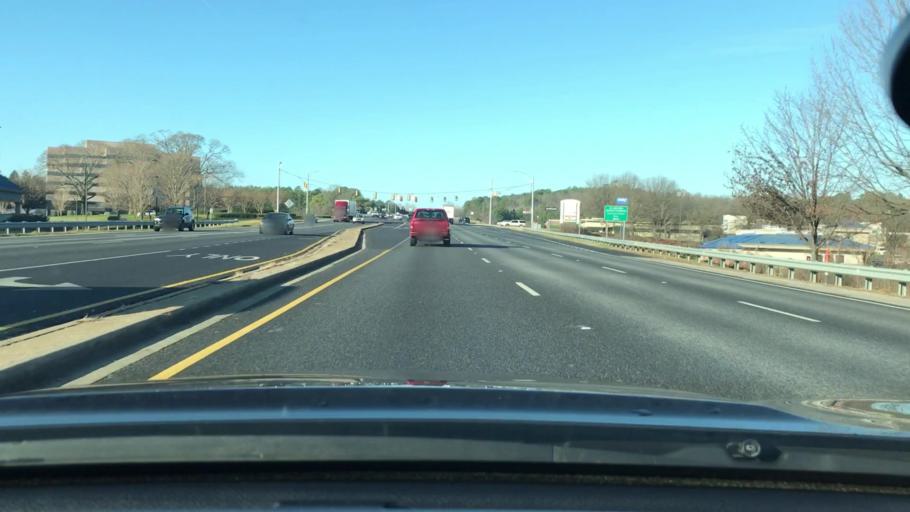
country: US
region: Alabama
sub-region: Shelby County
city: Lake Purdy
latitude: 33.4188
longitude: -86.6796
